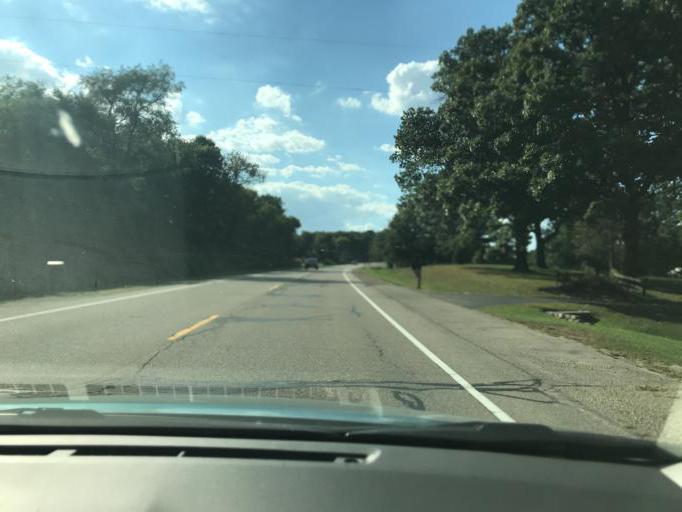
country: US
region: Wisconsin
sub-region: Rock County
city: Orfordville
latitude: 42.5257
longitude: -89.2178
